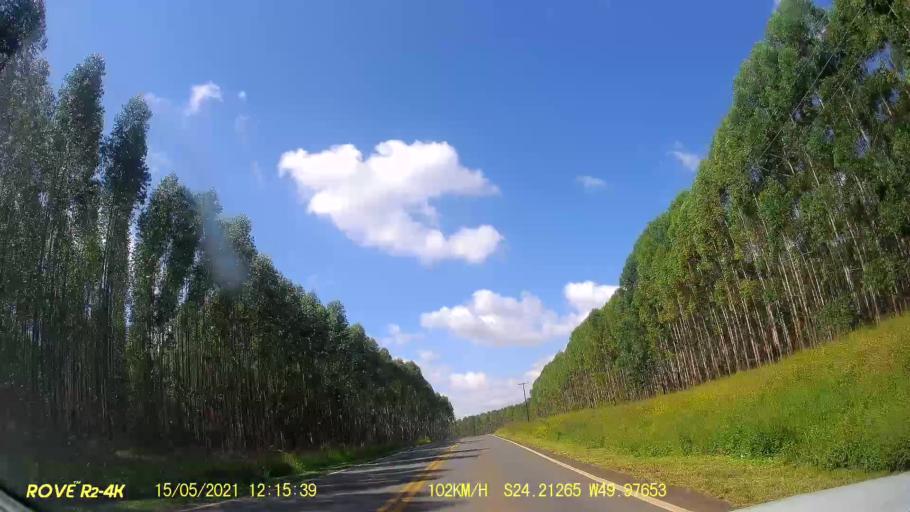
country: BR
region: Parana
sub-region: Jaguariaiva
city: Jaguariaiva
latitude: -24.2126
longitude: -49.9765
